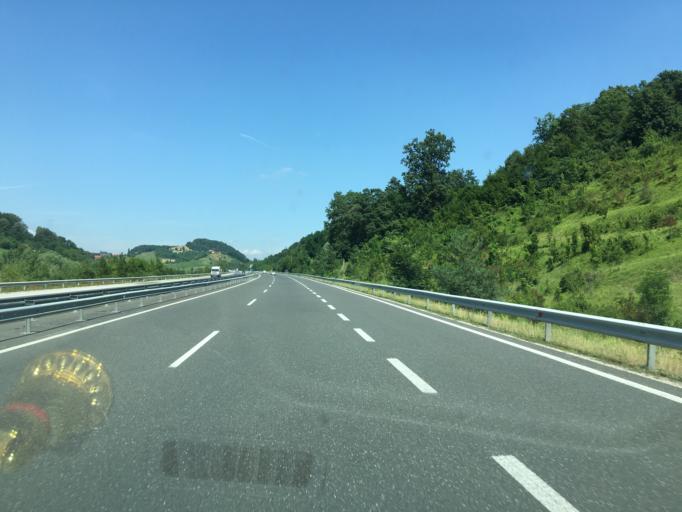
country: SI
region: Sentilj
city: Sentilj v Slov. Goricah
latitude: 46.6543
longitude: 15.6484
